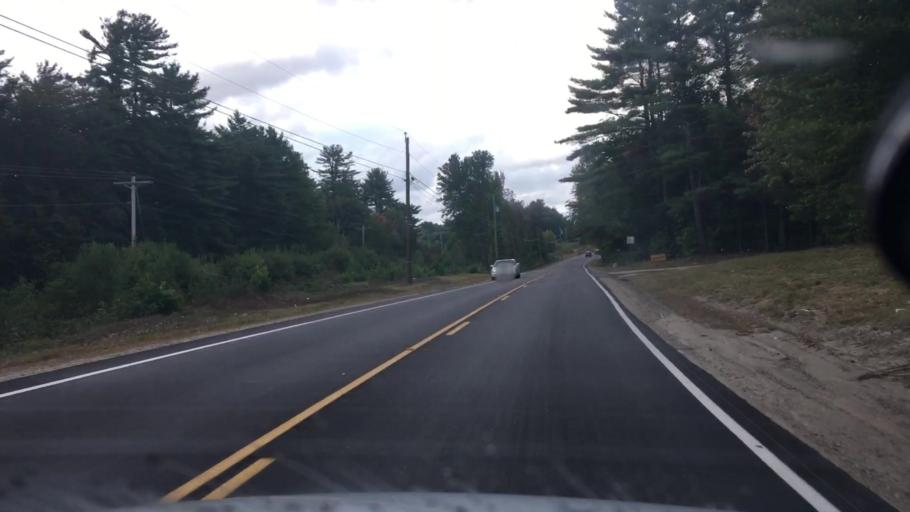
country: US
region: New Hampshire
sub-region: Carroll County
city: Sanbornville
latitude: 43.5386
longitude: -71.0270
